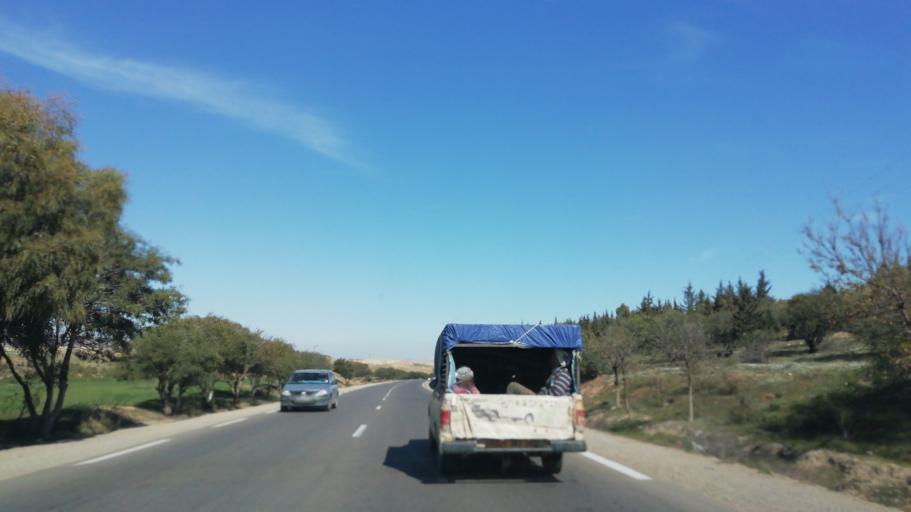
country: DZ
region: Mascara
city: Oued el Abtal
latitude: 35.4347
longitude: 0.4935
